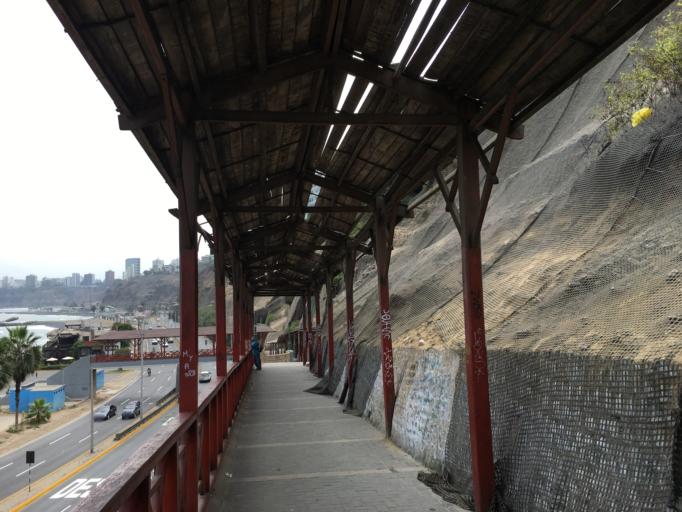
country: PE
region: Lima
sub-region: Lima
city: Surco
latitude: -12.1502
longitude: -77.0242
